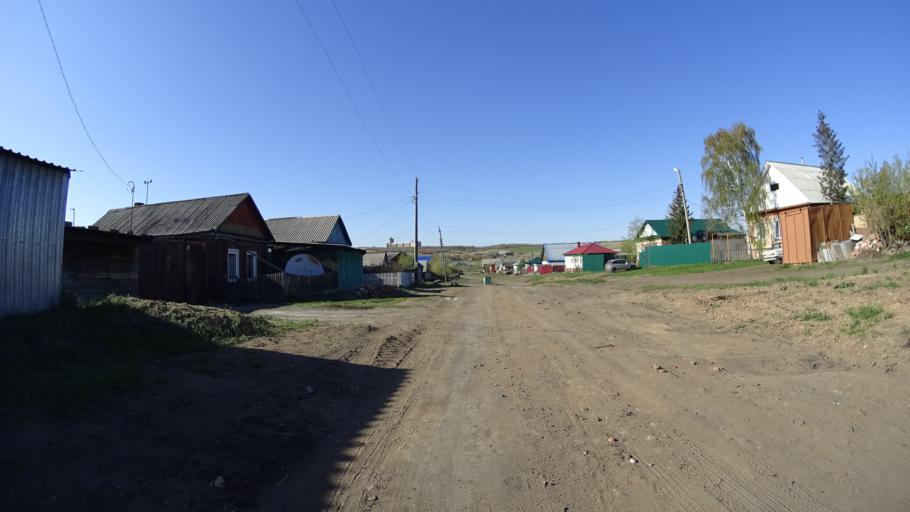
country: RU
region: Chelyabinsk
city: Troitsk
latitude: 54.0911
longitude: 61.5999
